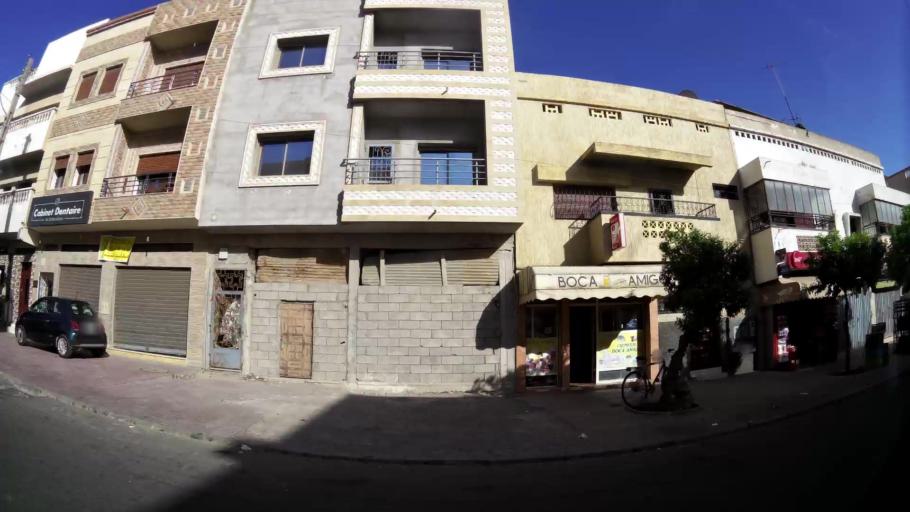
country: MA
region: Souss-Massa-Draa
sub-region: Agadir-Ida-ou-Tnan
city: Agadir
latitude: 30.4303
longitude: -9.5807
